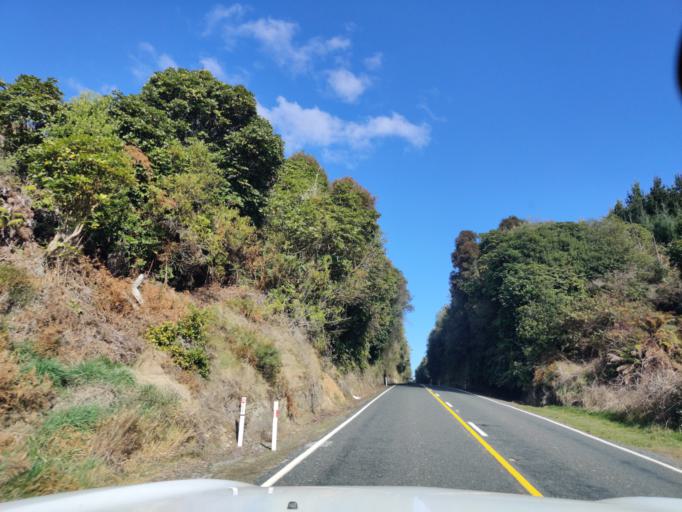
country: NZ
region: Waikato
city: Turangi
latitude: -38.7065
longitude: 175.6755
